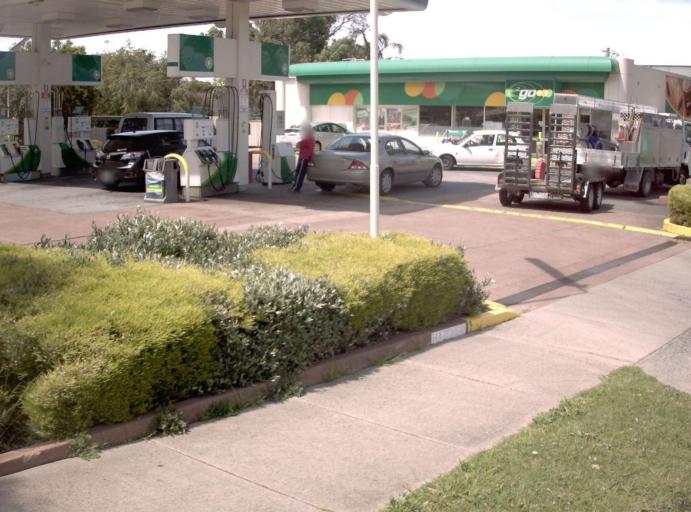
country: AU
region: Victoria
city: Burwood East
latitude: -37.8601
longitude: 145.1508
